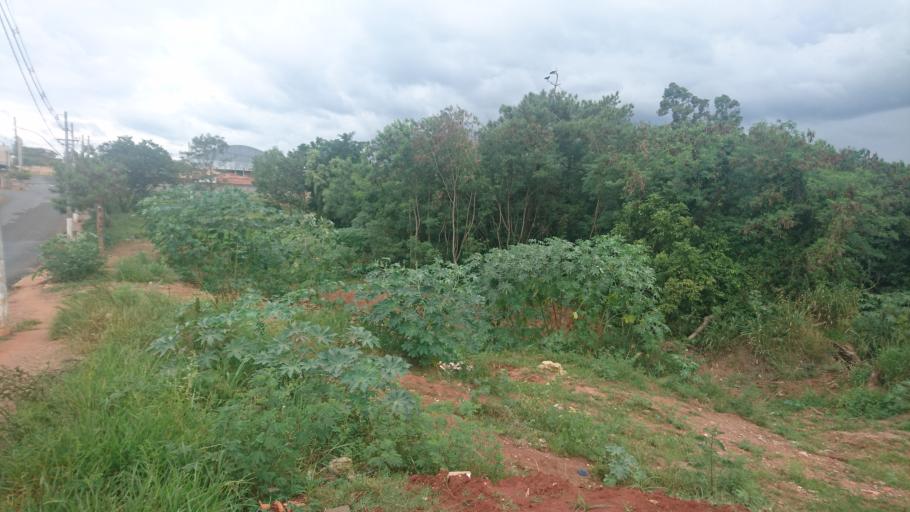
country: BR
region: Sao Paulo
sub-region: Casa Branca
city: Casa Branca
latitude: -21.7637
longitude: -47.0785
